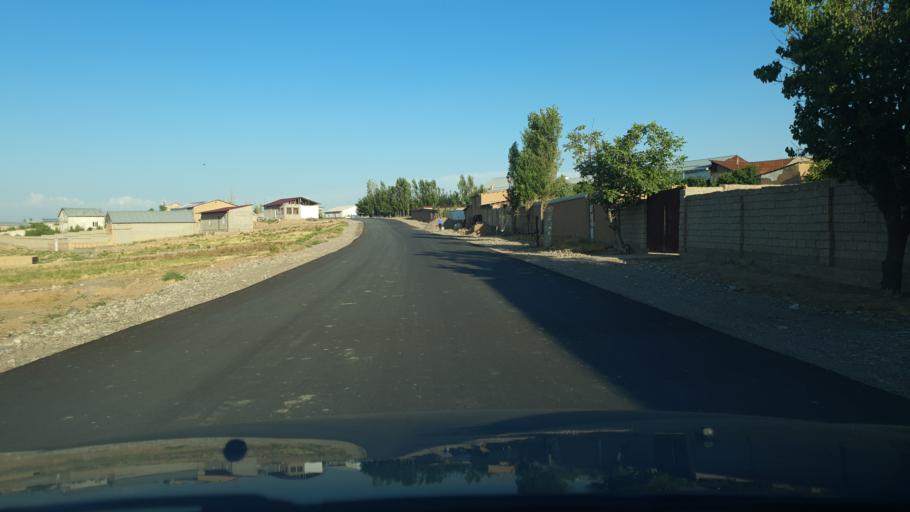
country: UZ
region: Toshkent
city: Salor
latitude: 41.4574
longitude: 69.3962
